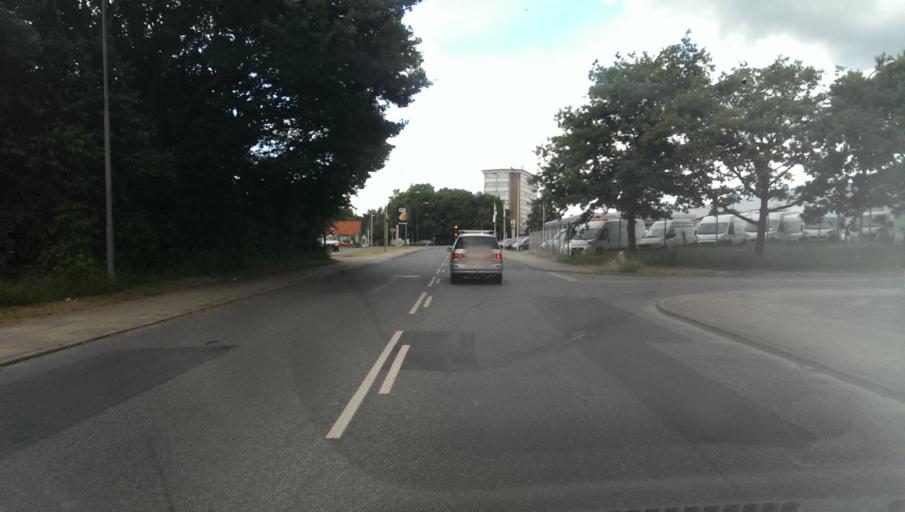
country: DK
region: South Denmark
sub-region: Esbjerg Kommune
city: Esbjerg
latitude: 55.4776
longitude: 8.4940
